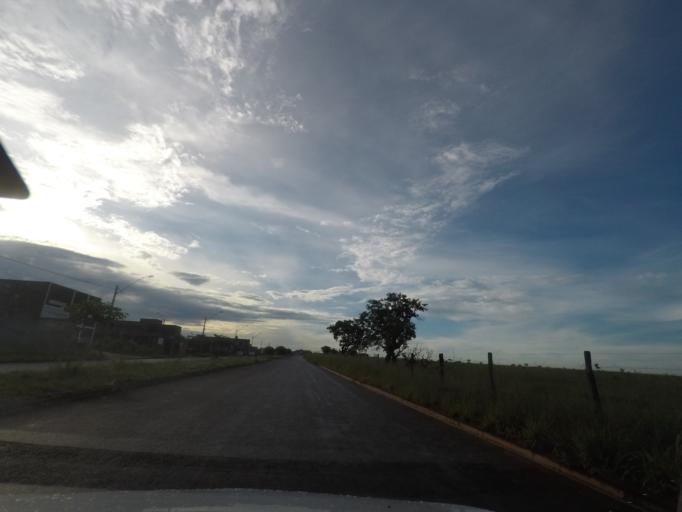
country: BR
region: Goias
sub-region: Trindade
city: Trindade
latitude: -16.7483
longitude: -49.3861
